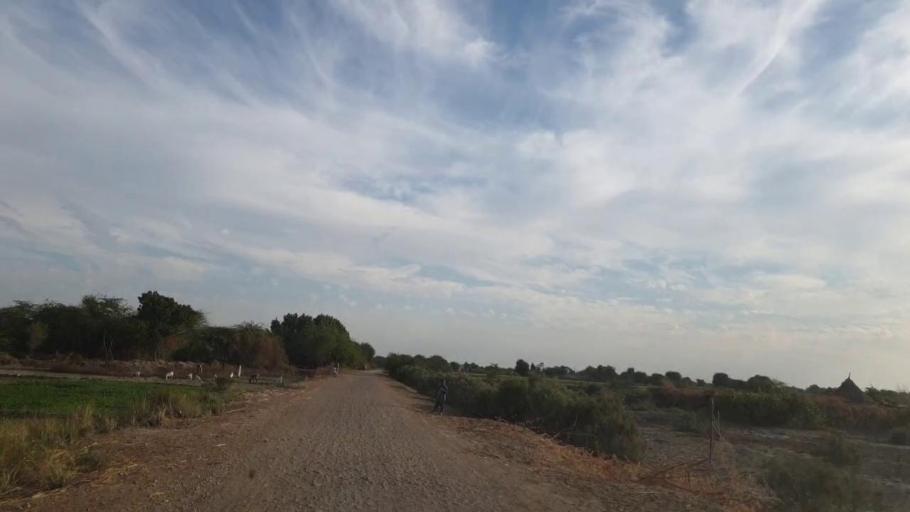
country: PK
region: Sindh
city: Pithoro
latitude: 25.6480
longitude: 69.2910
